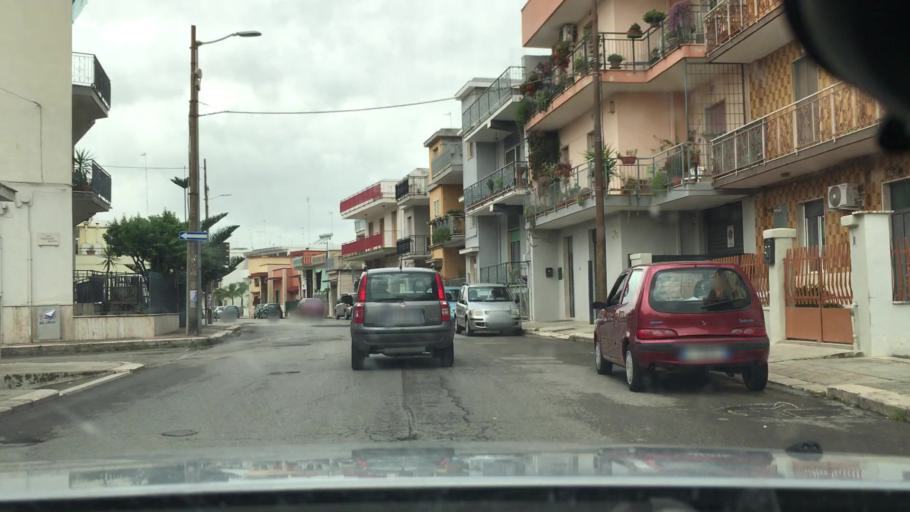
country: IT
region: Apulia
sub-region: Provincia di Bari
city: Capurso
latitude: 41.0470
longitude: 16.9275
